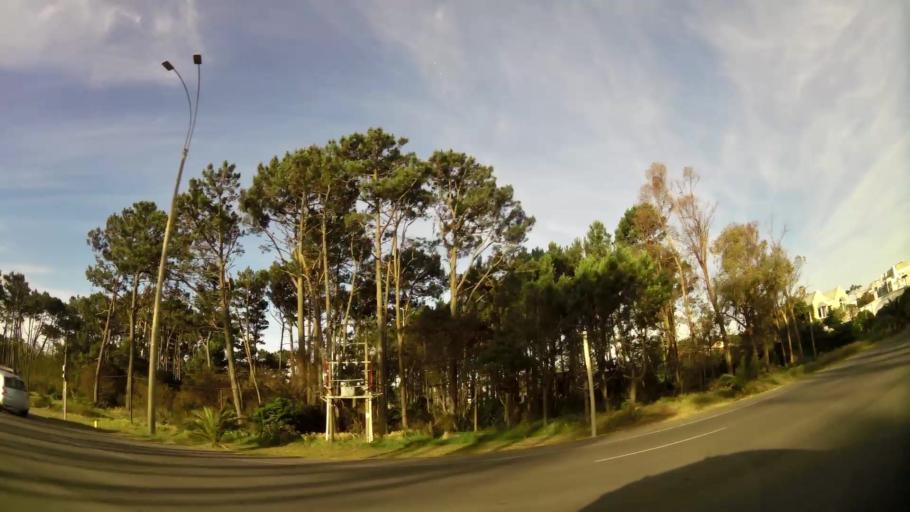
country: UY
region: Maldonado
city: Maldonado
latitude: -34.9072
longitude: -55.0205
